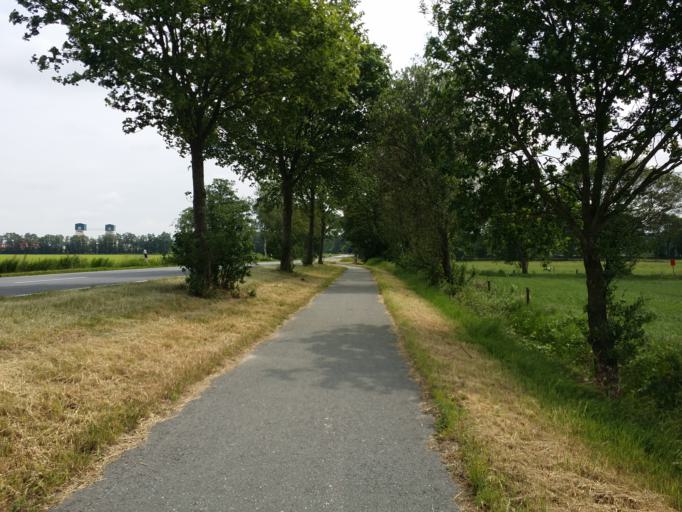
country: DE
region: Lower Saxony
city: Friedeburg
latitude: 53.4206
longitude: 7.8729
